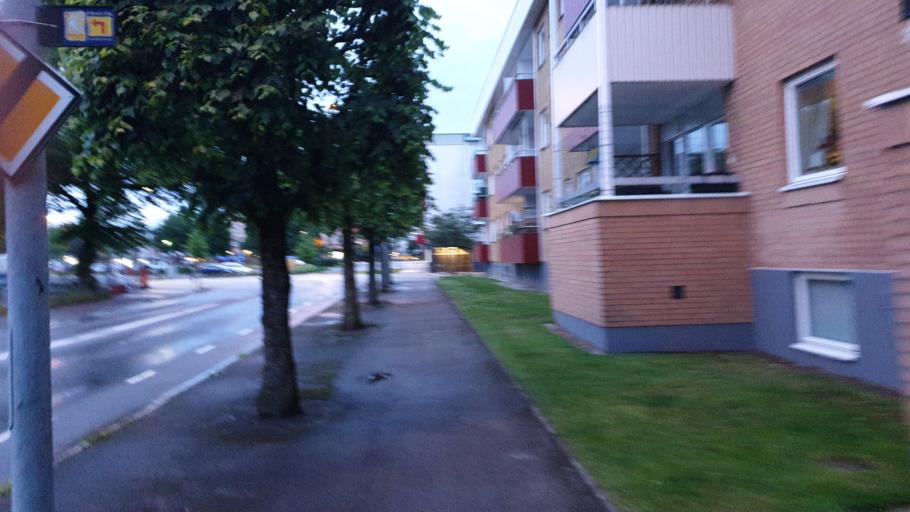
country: SE
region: Kronoberg
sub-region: Ljungby Kommun
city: Ljungby
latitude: 56.8312
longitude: 13.9402
